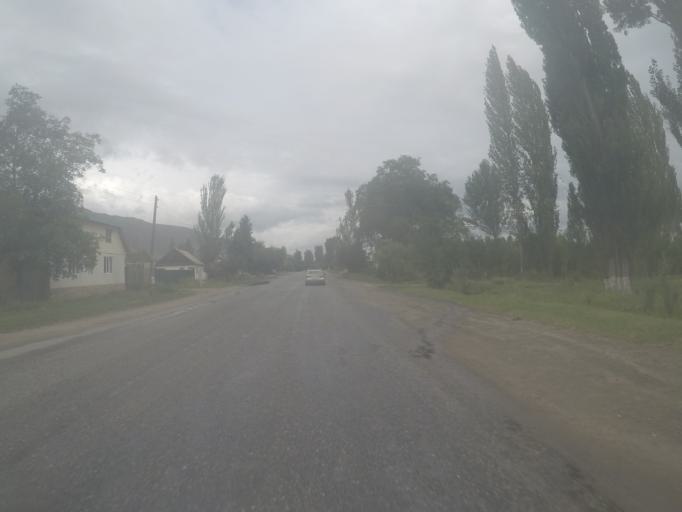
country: KG
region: Ysyk-Koel
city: Tyup
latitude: 42.7383
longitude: 78.0028
